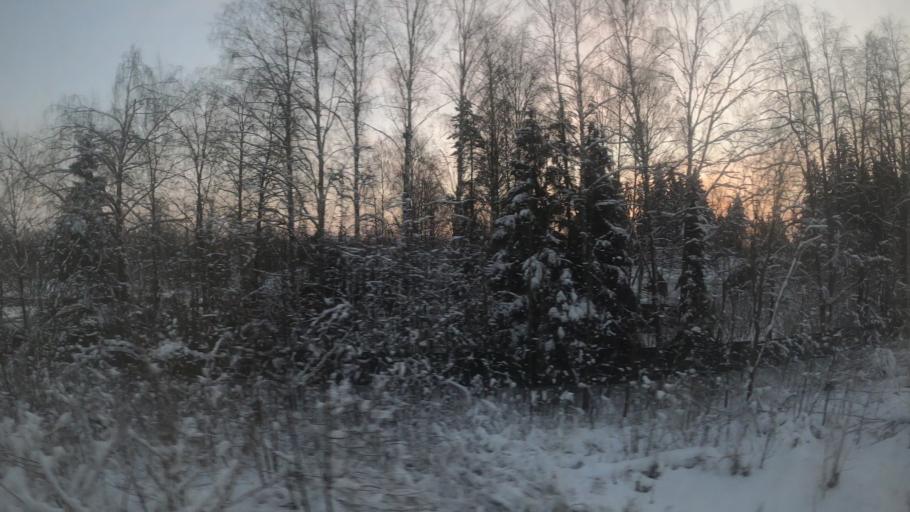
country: RU
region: Moskovskaya
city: Yermolino
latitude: 56.1284
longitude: 37.5197
